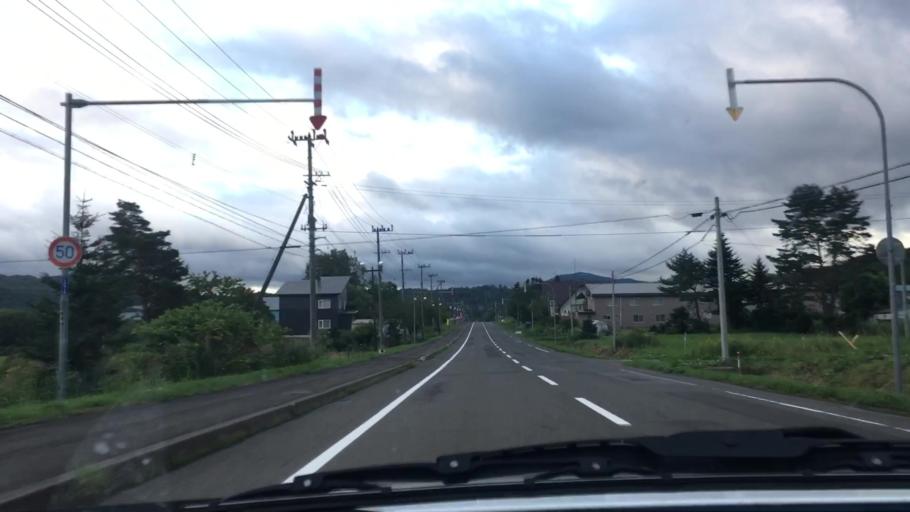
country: JP
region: Hokkaido
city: Shimo-furano
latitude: 42.9949
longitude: 142.4026
